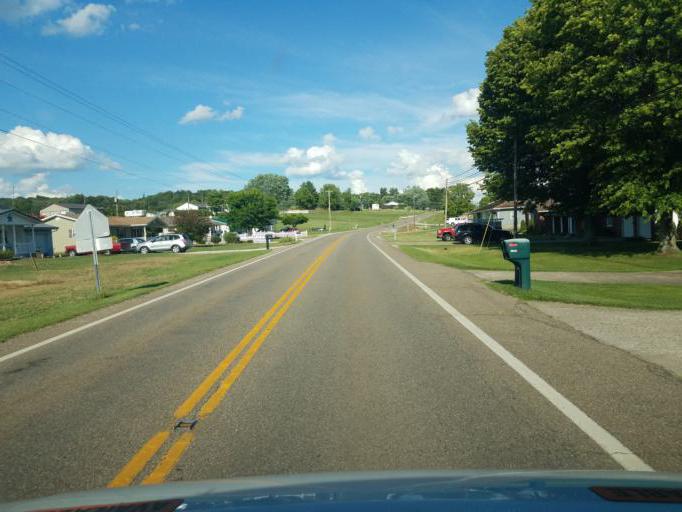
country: US
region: Ohio
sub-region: Gallia County
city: Gallipolis
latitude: 38.8004
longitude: -82.2604
